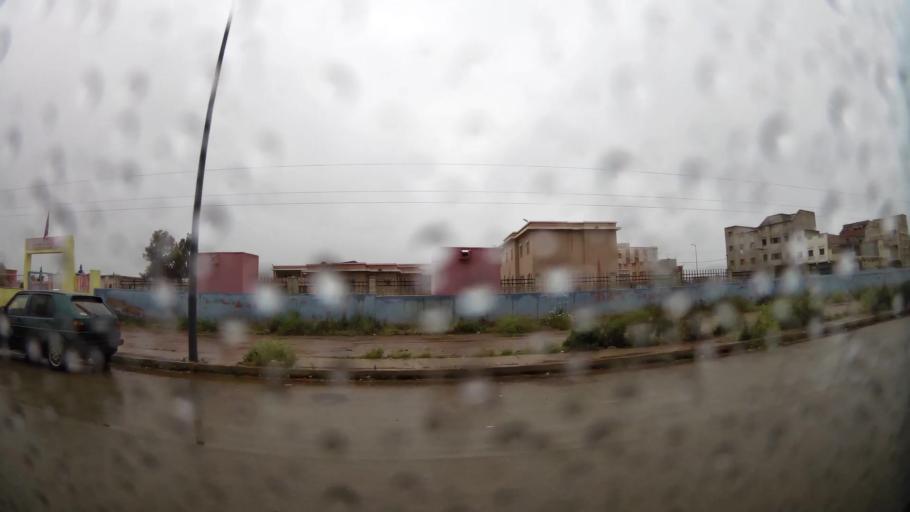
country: MA
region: Oriental
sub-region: Nador
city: Boudinar
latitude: 35.1144
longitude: -3.6437
